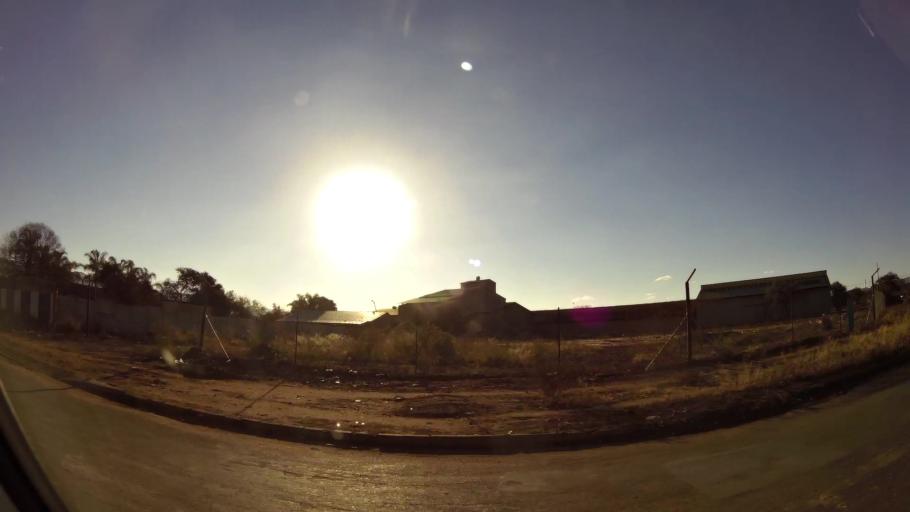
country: ZA
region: Limpopo
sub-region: Waterberg District Municipality
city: Mokopane
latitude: -24.1723
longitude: 29.0020
